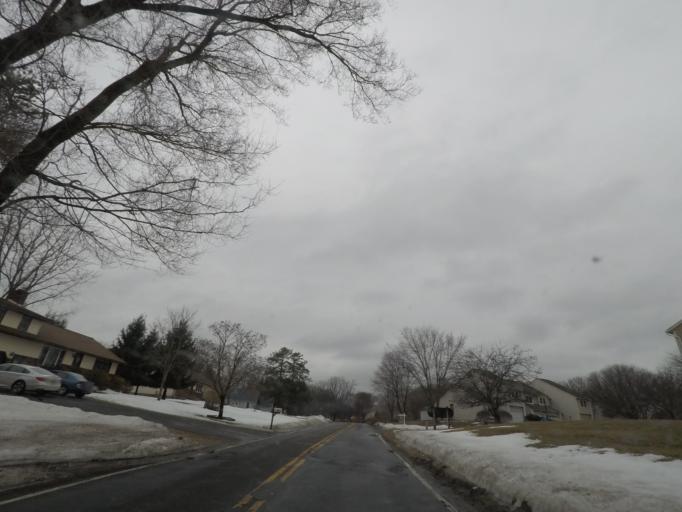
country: US
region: New York
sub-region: Albany County
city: Westmere
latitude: 42.6946
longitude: -73.8577
